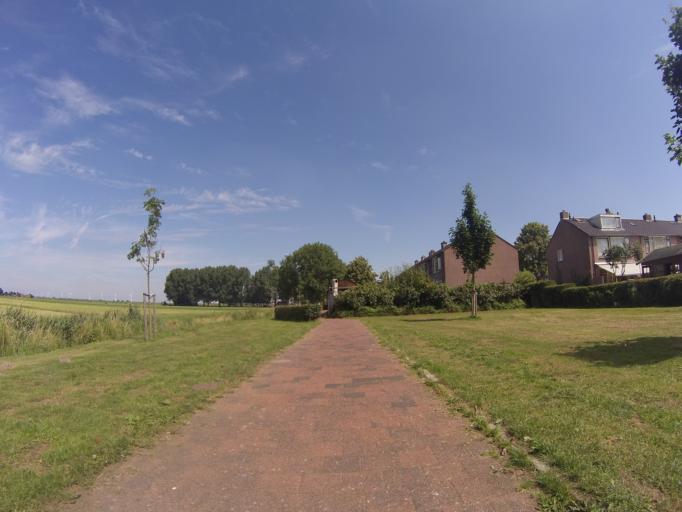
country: NL
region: Utrecht
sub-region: Gemeente Bunschoten
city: Spakenburg
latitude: 52.2555
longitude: 5.3690
